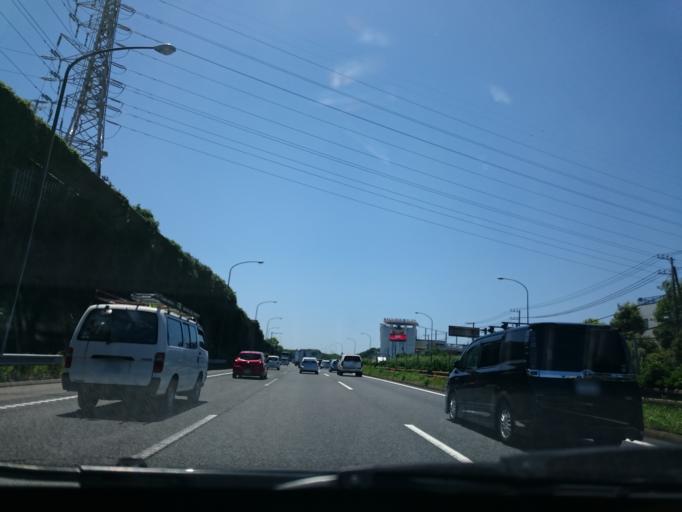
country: JP
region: Kanagawa
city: Minami-rinkan
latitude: 35.4962
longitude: 139.4739
